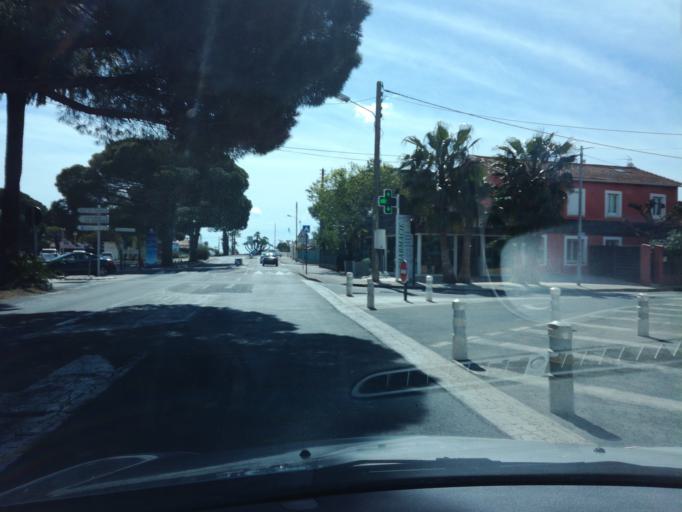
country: FR
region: Provence-Alpes-Cote d'Azur
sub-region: Departement du Var
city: Hyeres
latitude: 43.1065
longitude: 6.1750
